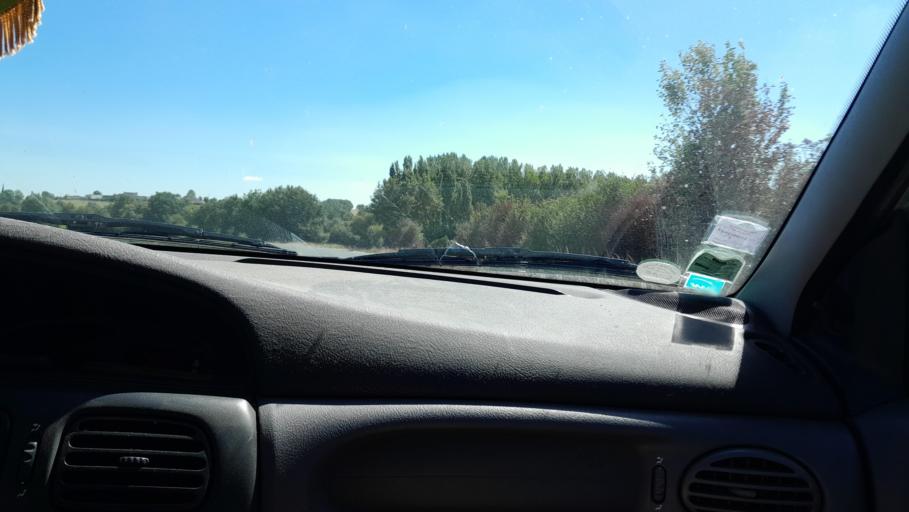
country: FR
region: Pays de la Loire
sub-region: Departement de la Loire-Atlantique
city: Saint-Mars-la-Jaille
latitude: 47.5902
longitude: -1.1972
